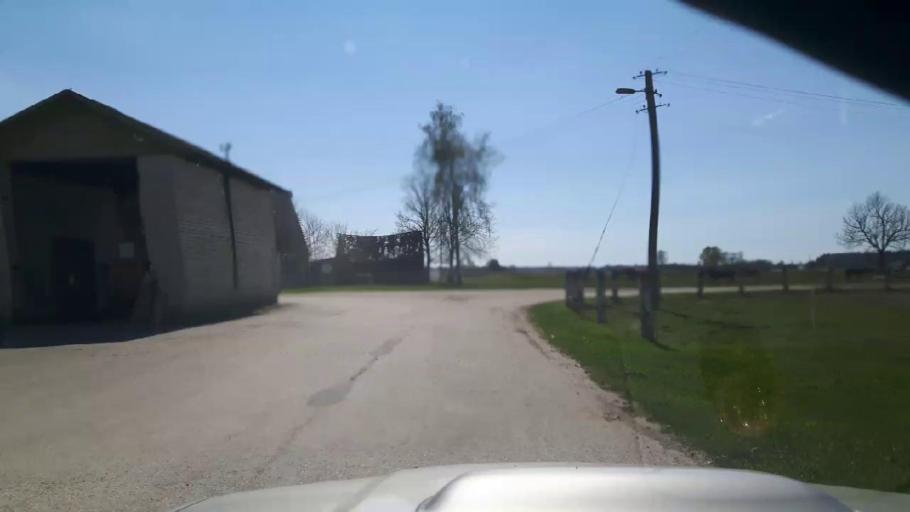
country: EE
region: Paernumaa
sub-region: Tootsi vald
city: Tootsi
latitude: 58.4793
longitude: 24.8159
